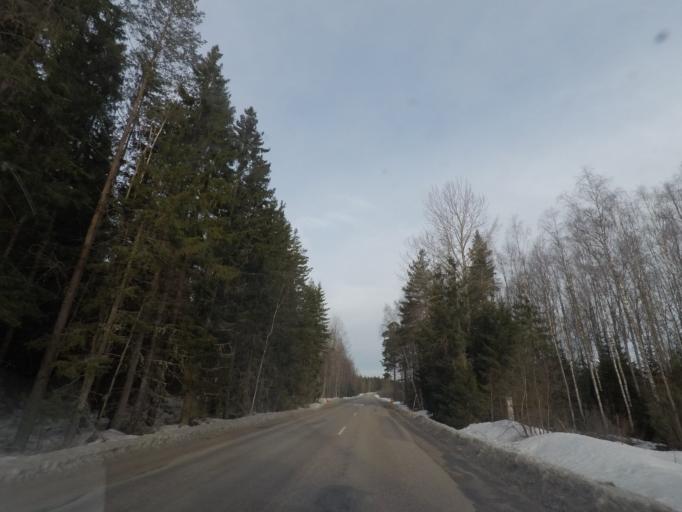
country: SE
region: Vaestmanland
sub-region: Surahammars Kommun
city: Surahammar
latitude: 59.7563
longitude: 16.3090
